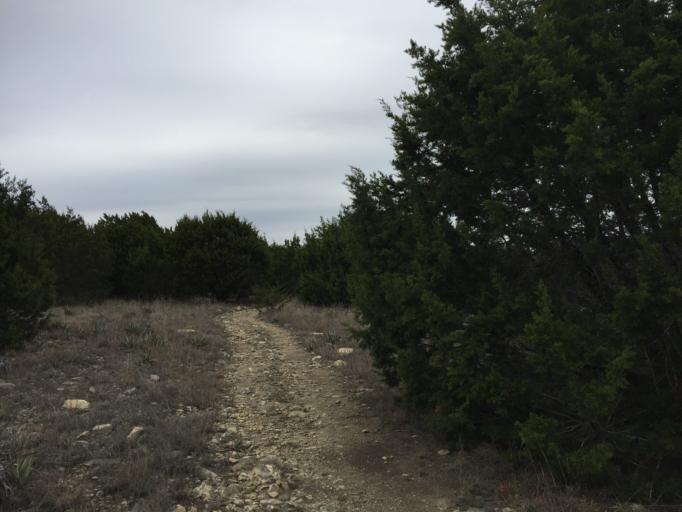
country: US
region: Texas
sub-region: Bell County
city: Fort Hood
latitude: 31.1192
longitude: -97.8169
